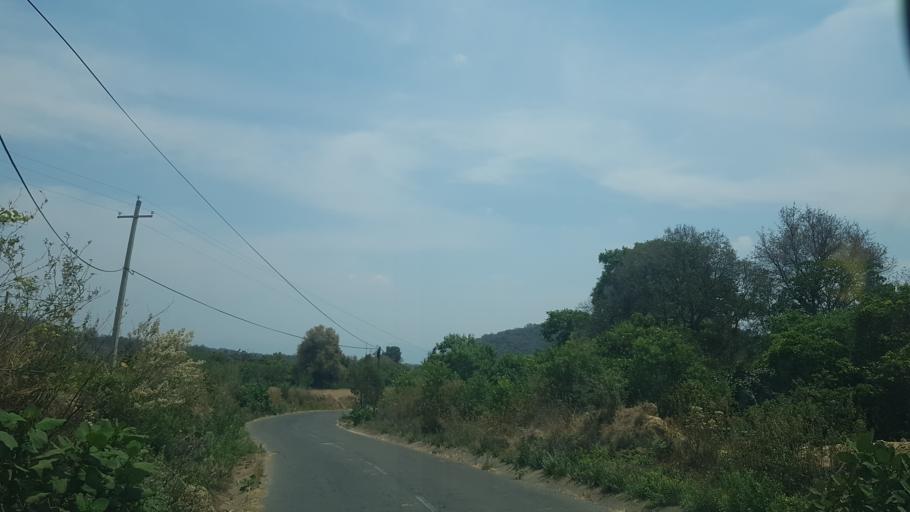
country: MX
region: Puebla
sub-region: Tochimilco
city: Santa Cruz Cuautomatitla
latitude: 18.8729
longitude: -98.6164
